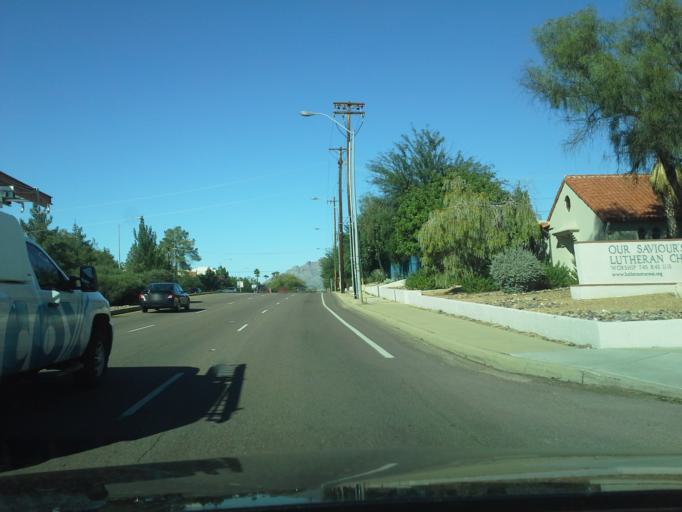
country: US
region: Arizona
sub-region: Pima County
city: Tucson
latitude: 32.2373
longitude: -110.9439
